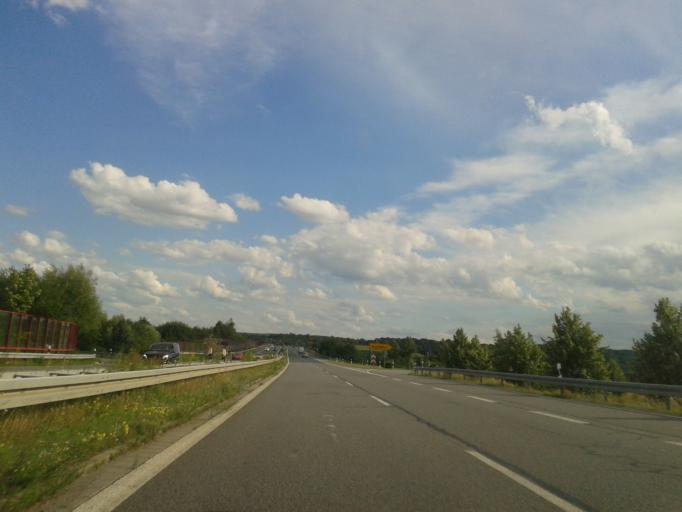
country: DE
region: Saxony
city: Pirna
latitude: 50.9702
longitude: 13.9150
